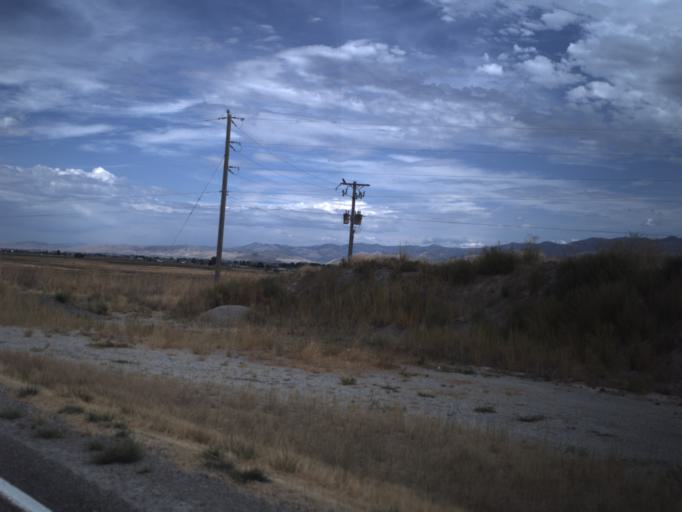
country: US
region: Utah
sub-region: Cache County
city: Benson
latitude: 41.8753
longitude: -111.9485
